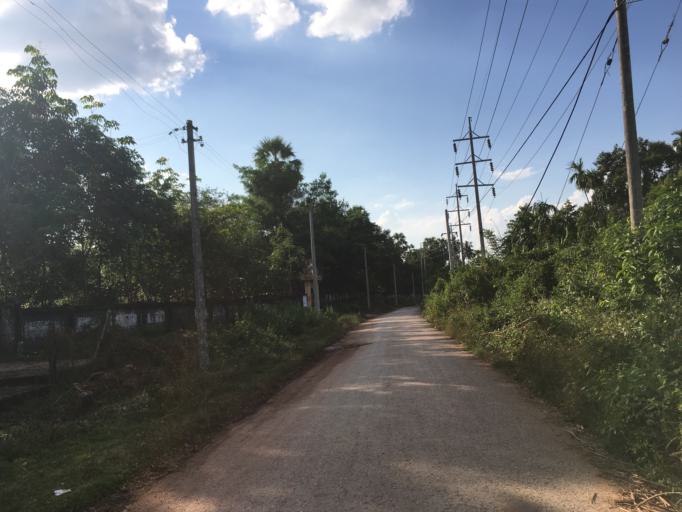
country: MM
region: Mon
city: Mawlamyine
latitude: 16.4282
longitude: 97.6249
